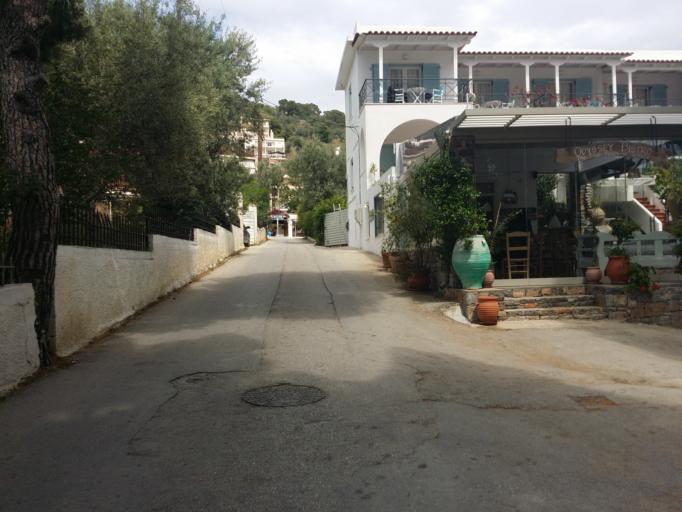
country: GR
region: Attica
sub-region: Nomos Piraios
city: Poros
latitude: 37.5089
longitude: 23.4701
